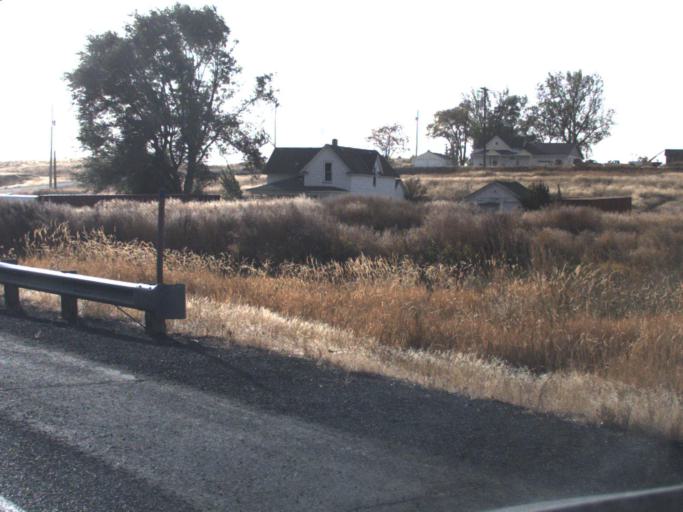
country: US
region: Washington
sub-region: Lincoln County
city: Davenport
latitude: 47.4845
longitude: -118.2556
